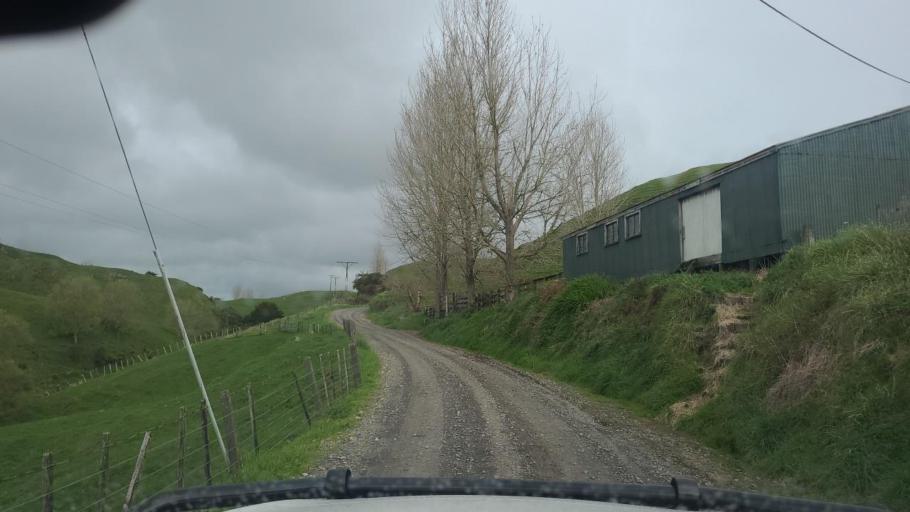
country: NZ
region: Taranaki
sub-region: South Taranaki District
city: Eltham
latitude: -39.2580
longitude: 174.4098
